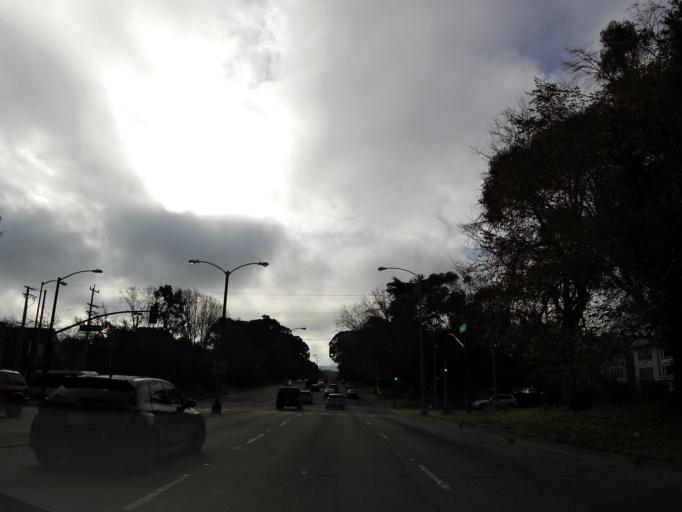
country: US
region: California
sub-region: San Francisco County
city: San Francisco
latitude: 37.7849
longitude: -122.4727
